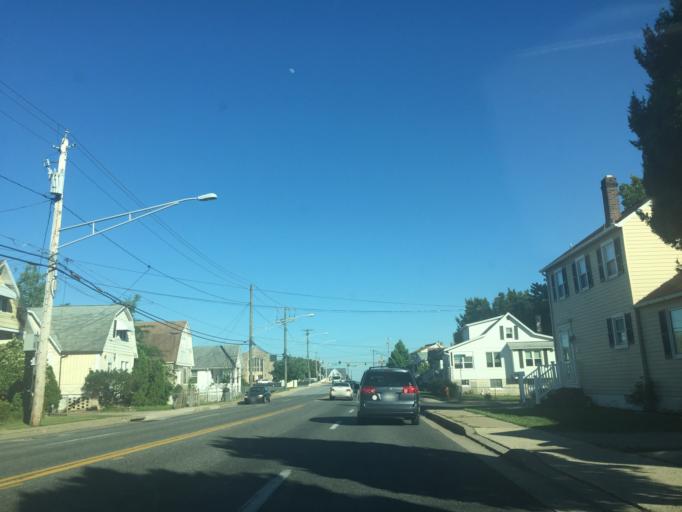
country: US
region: Maryland
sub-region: Baltimore County
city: Parkville
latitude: 39.3848
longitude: -76.5362
